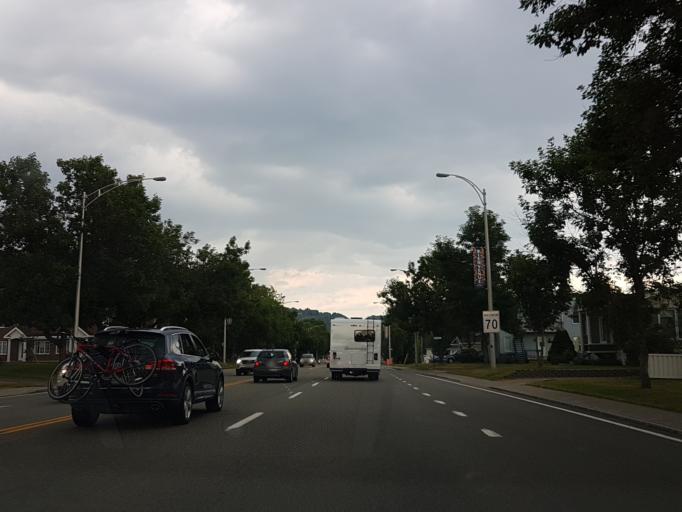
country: CA
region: Quebec
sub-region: Capitale-Nationale
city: Beaupre
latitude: 47.0461
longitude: -70.8926
